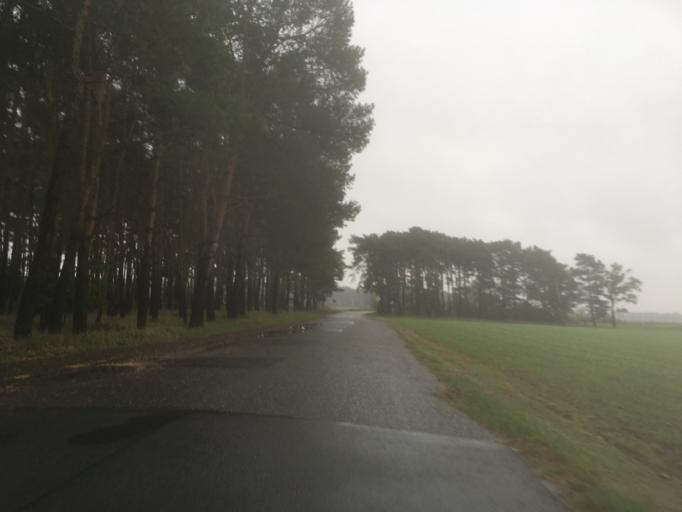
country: DE
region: Brandenburg
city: Schlepzig
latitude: 52.0164
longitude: 13.9432
